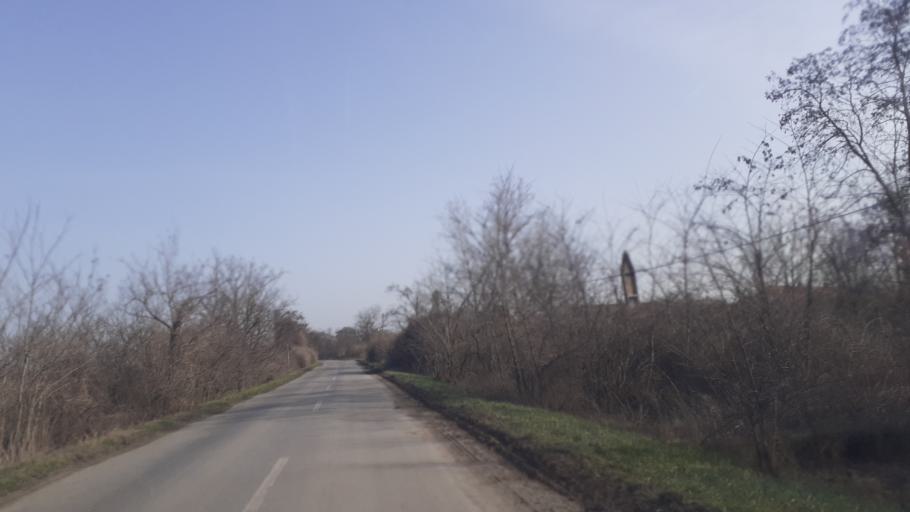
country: HU
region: Bacs-Kiskun
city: Tass
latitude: 47.0213
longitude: 18.9915
